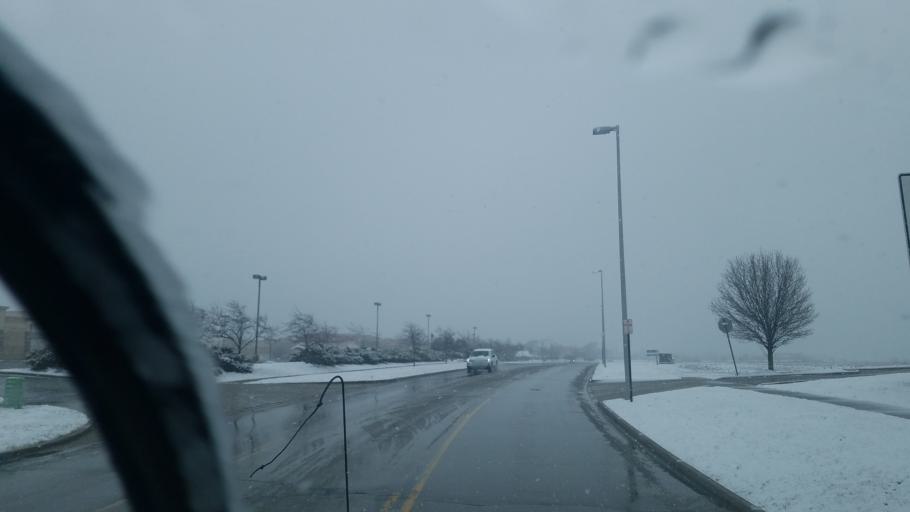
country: US
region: Ohio
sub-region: Union County
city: Marysville
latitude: 40.2316
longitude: -83.3420
